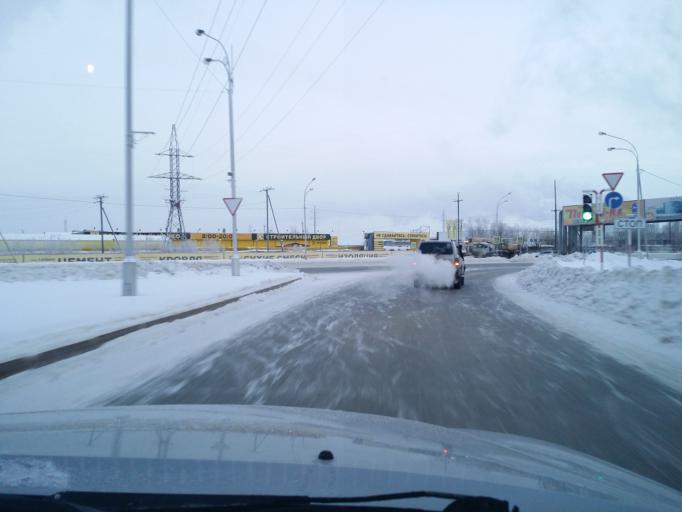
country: RU
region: Khanty-Mansiyskiy Avtonomnyy Okrug
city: Nizhnevartovsk
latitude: 60.9479
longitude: 76.5286
